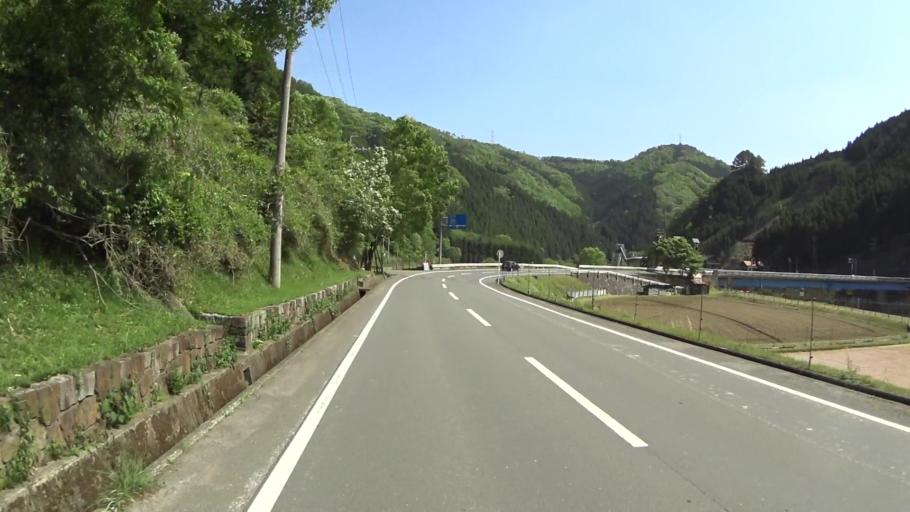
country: JP
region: Kyoto
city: Kameoka
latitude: 35.1491
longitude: 135.5061
